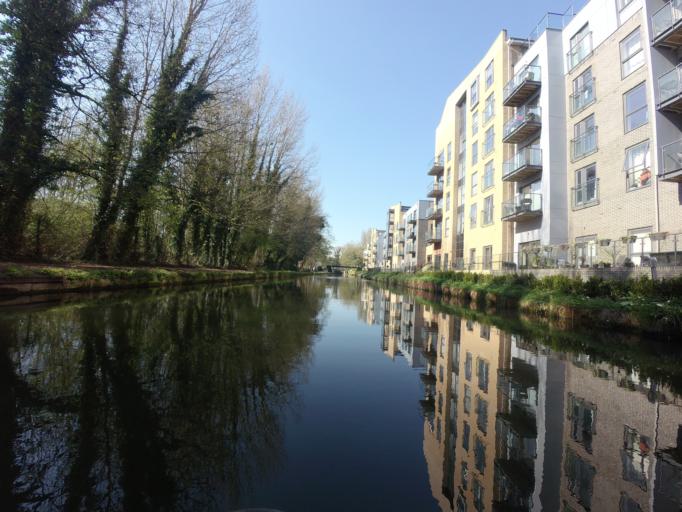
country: GB
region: England
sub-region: Hertfordshire
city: Kings Langley
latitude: 51.7283
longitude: -0.4530
